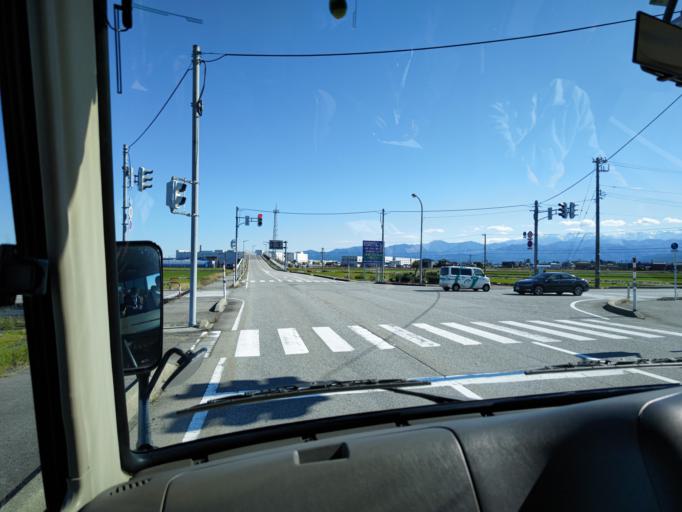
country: JP
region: Toyama
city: Nyuzen
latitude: 36.8909
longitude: 137.4243
